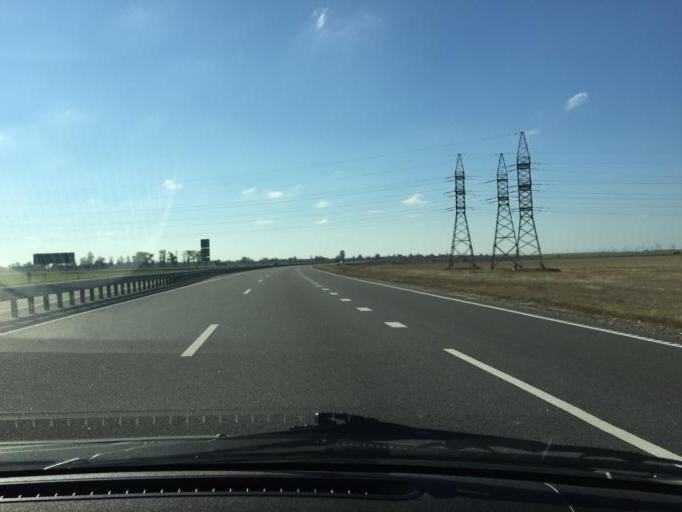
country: BY
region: Minsk
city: Slutsk
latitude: 53.0527
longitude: 27.5355
